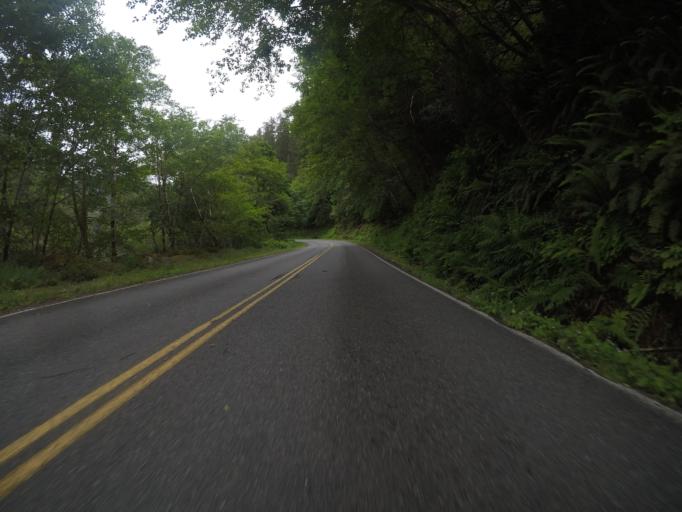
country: US
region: California
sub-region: Del Norte County
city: Bertsch-Oceanview
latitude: 41.7818
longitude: -124.0221
